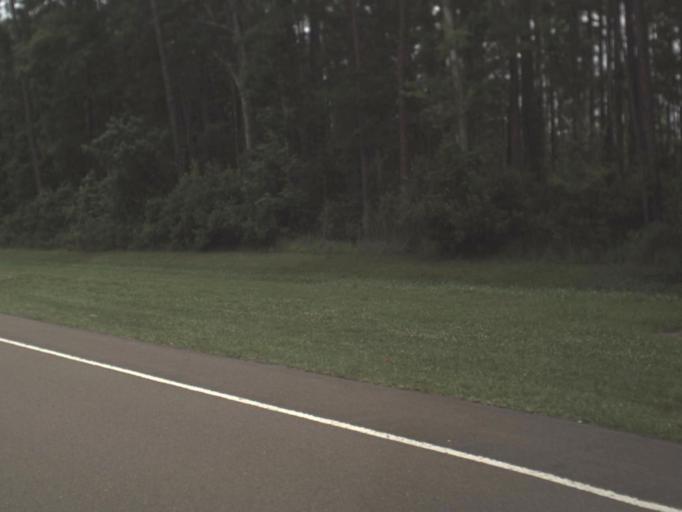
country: US
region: Florida
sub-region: Nassau County
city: Nassau Village-Ratliff
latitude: 30.4868
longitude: -81.6699
